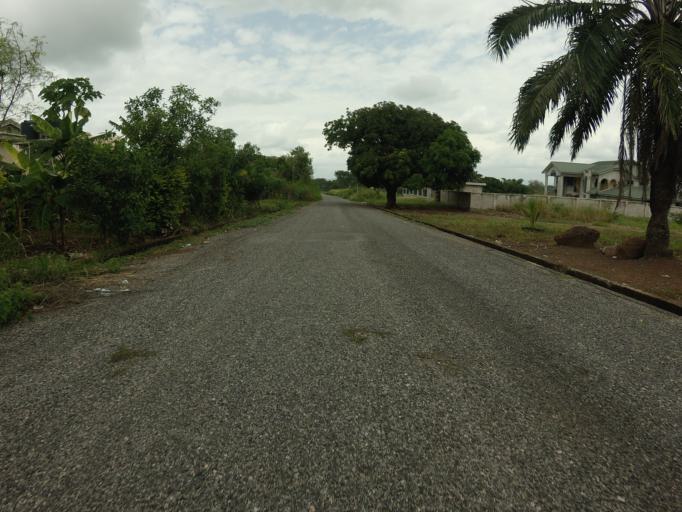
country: GH
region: Volta
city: Ho
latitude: 6.5917
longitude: 0.4638
